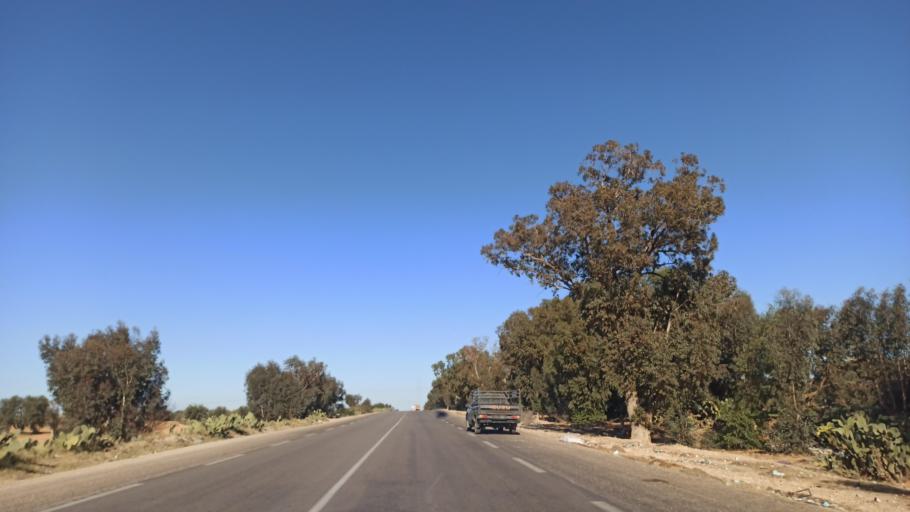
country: TN
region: Sidi Bu Zayd
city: Jilma
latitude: 35.1634
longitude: 9.3680
